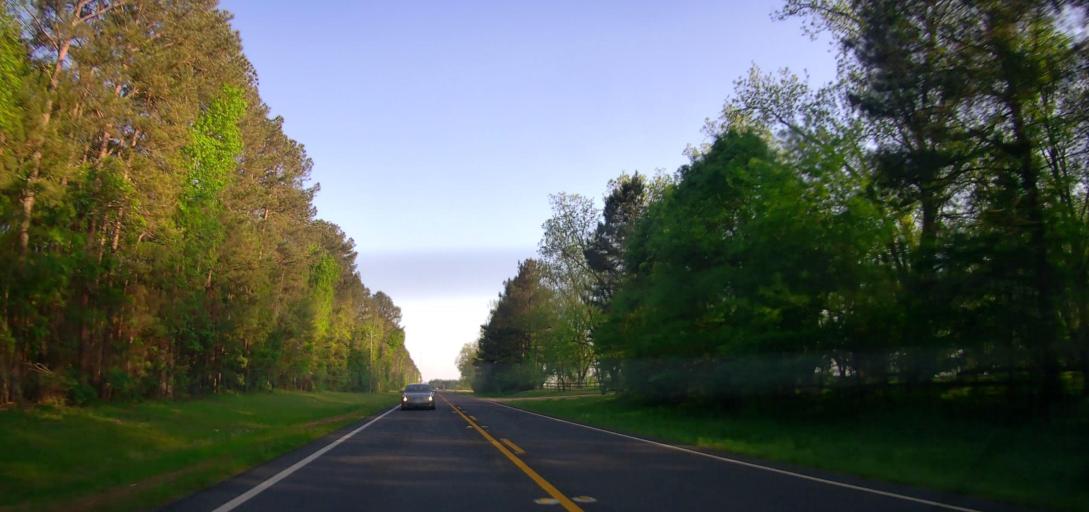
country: US
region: Georgia
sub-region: Jasper County
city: Monticello
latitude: 33.4576
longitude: -83.6319
